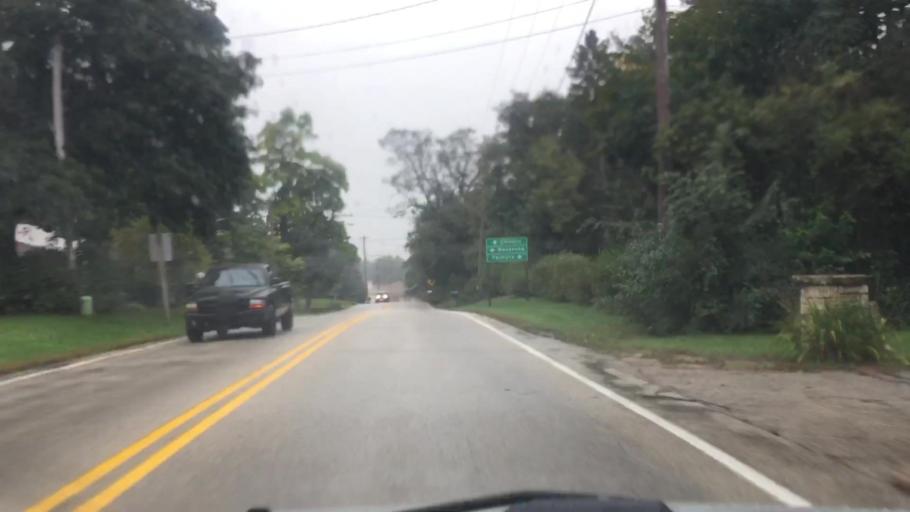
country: US
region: Wisconsin
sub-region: Waukesha County
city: Eagle
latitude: 42.8827
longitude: -88.4736
